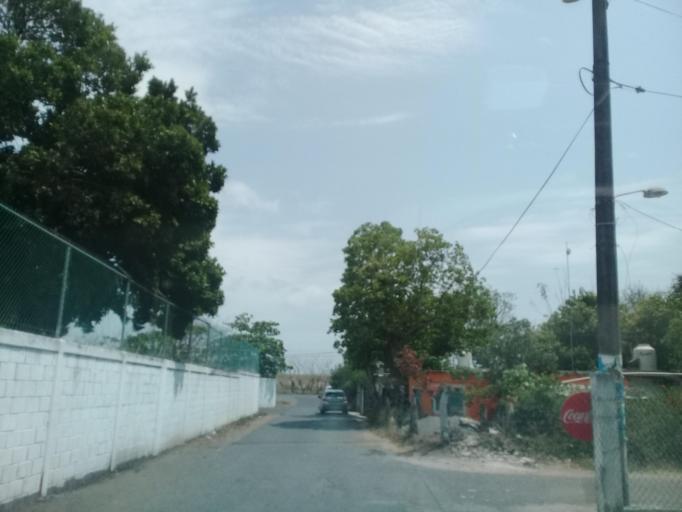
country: MX
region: Veracruz
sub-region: Veracruz
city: Delfino Victoria (Santa Fe)
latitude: 19.1743
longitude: -96.2744
